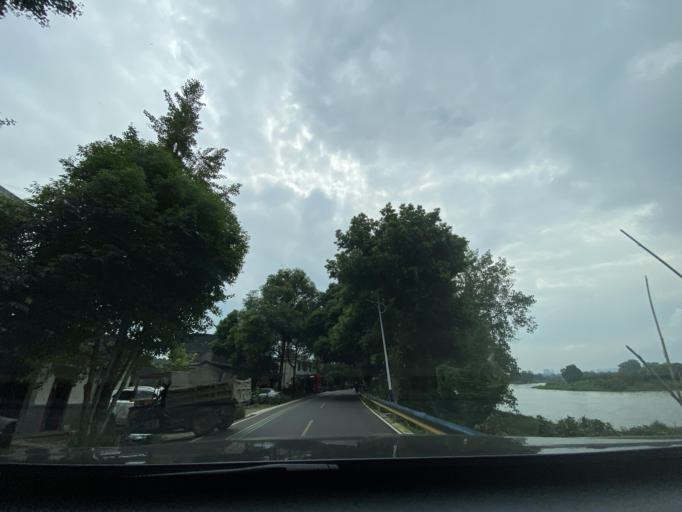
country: CN
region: Sichuan
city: Wujin
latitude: 30.3975
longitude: 103.9866
